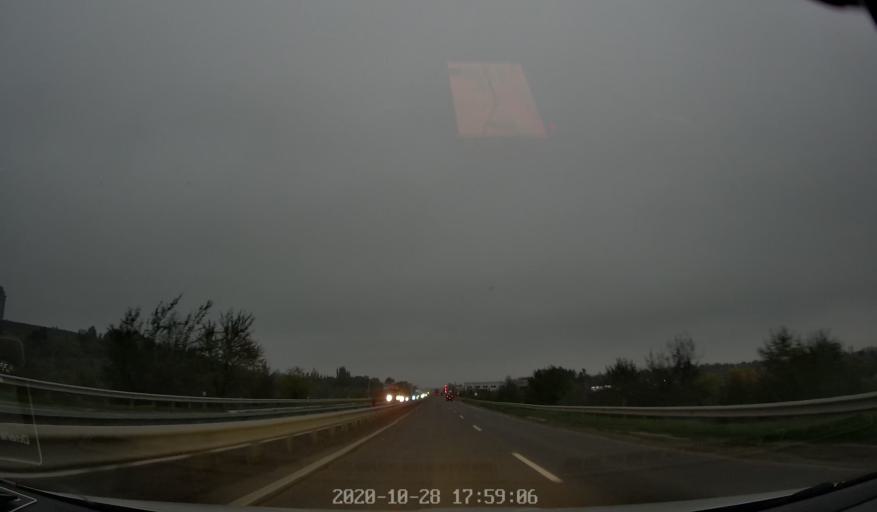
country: MD
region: Laloveni
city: Ialoveni
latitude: 46.9530
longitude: 28.7537
